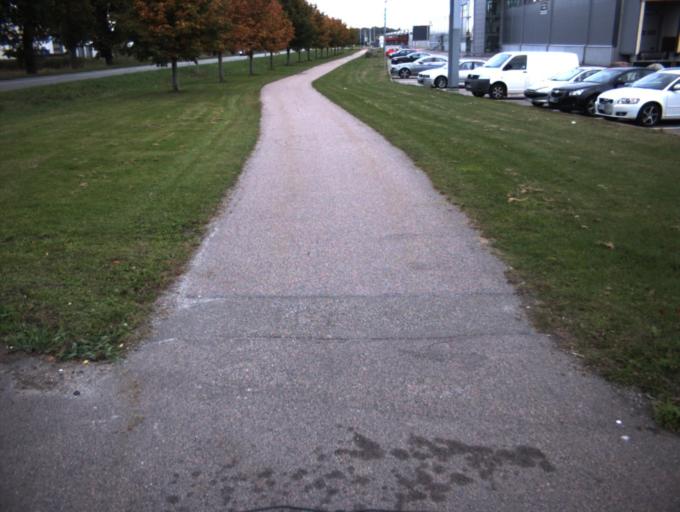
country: SE
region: Skane
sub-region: Helsingborg
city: Barslov
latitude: 56.0422
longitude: 12.7798
